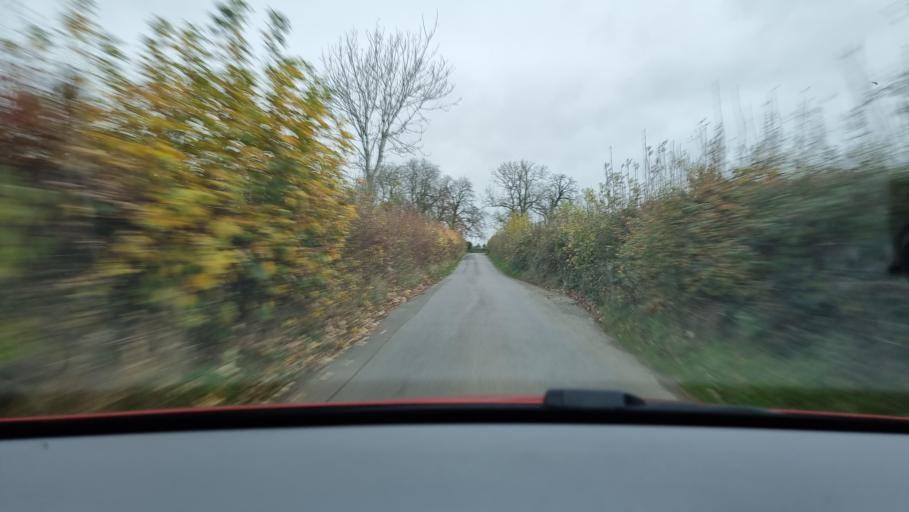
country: GB
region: England
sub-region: Oxfordshire
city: Woodstock
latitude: 51.8764
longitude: -1.3142
